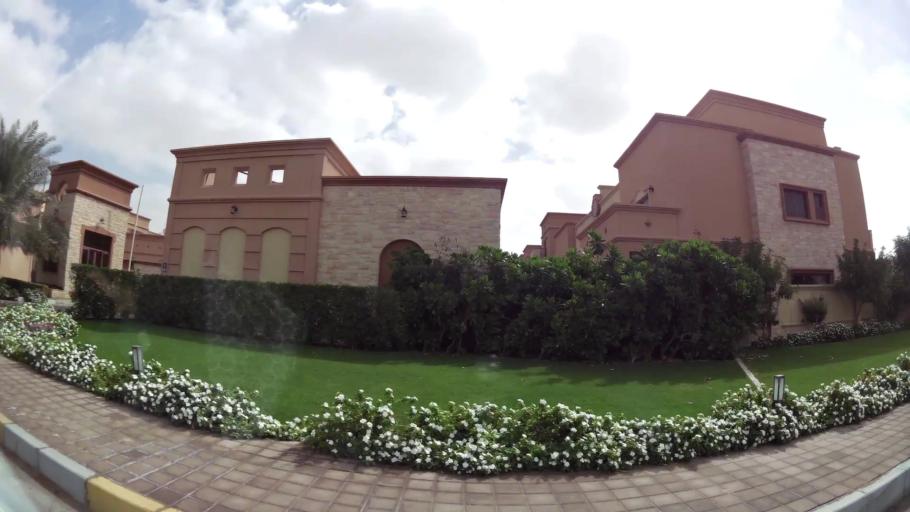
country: AE
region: Abu Dhabi
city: Abu Dhabi
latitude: 24.4127
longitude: 54.4937
